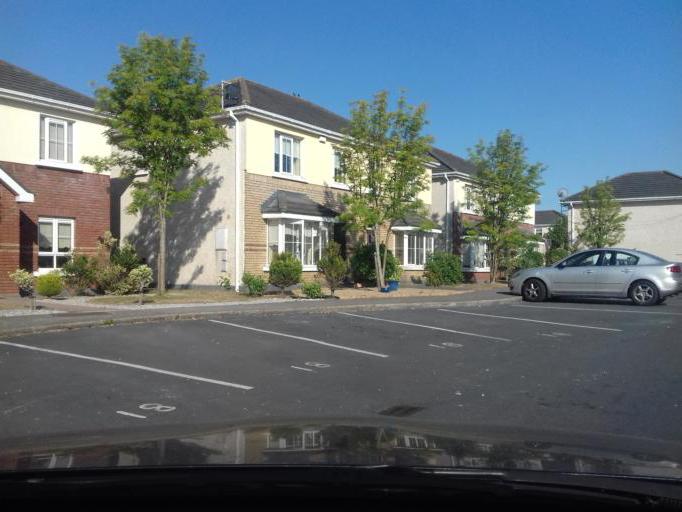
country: IE
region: Leinster
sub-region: Fingal County
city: Blanchardstown
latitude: 53.4219
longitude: -6.3947
